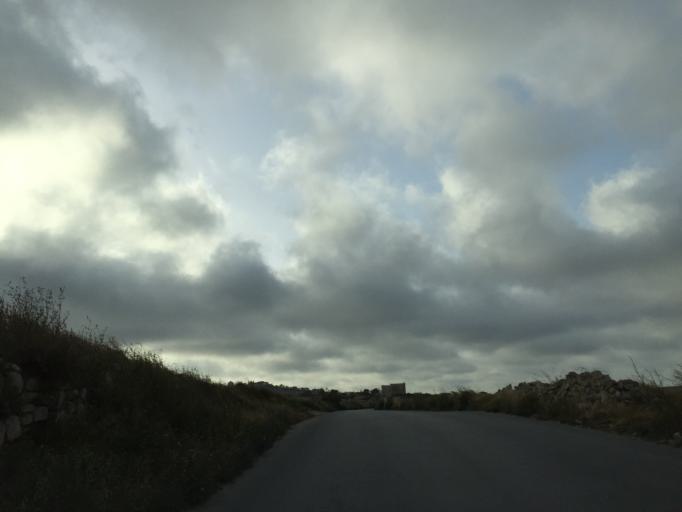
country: MT
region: Is-Siggiewi
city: Siggiewi
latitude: 35.8628
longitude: 14.4187
